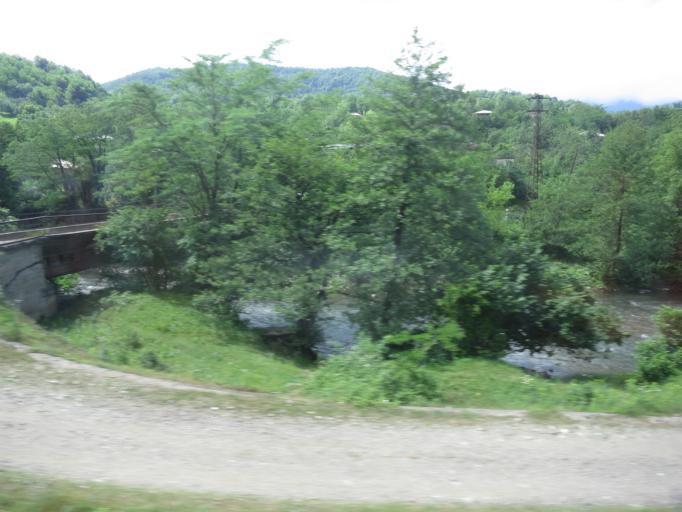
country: GE
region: Imereti
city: Kharagauli
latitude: 41.9986
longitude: 43.2350
